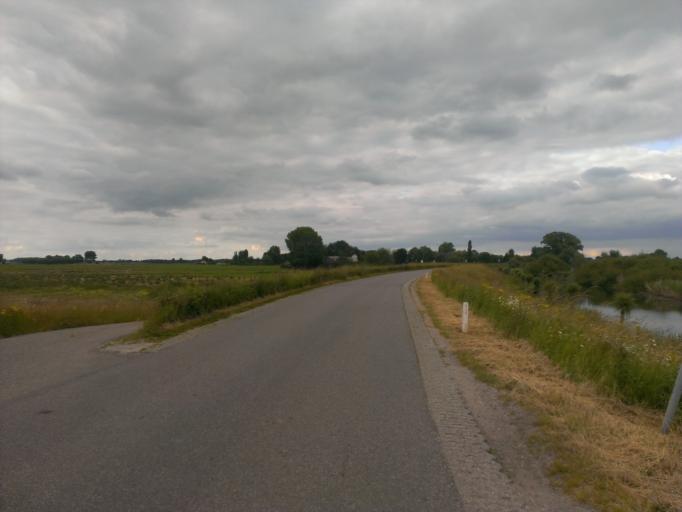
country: NL
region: Gelderland
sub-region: Gemeente Heerde
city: Heerde
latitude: 52.3733
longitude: 6.0770
